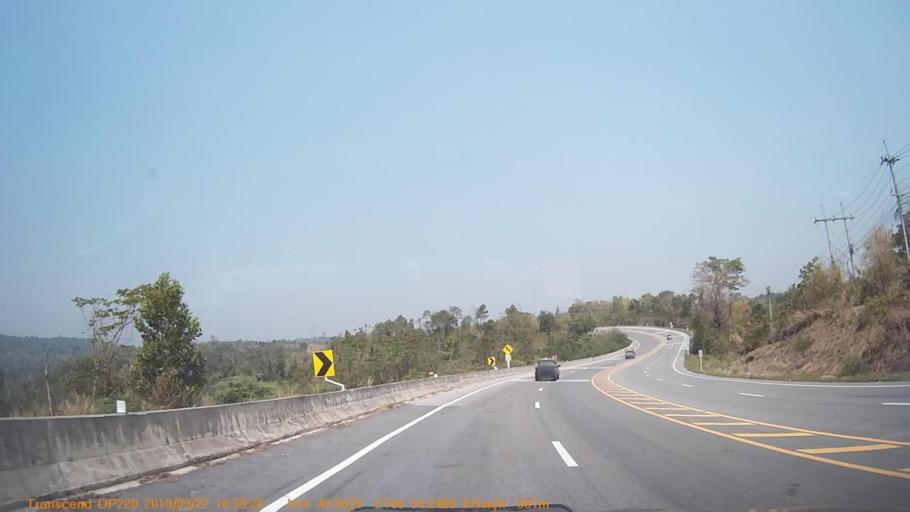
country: TH
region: Phetchabun
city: Khao Kho
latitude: 16.8255
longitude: 100.9036
